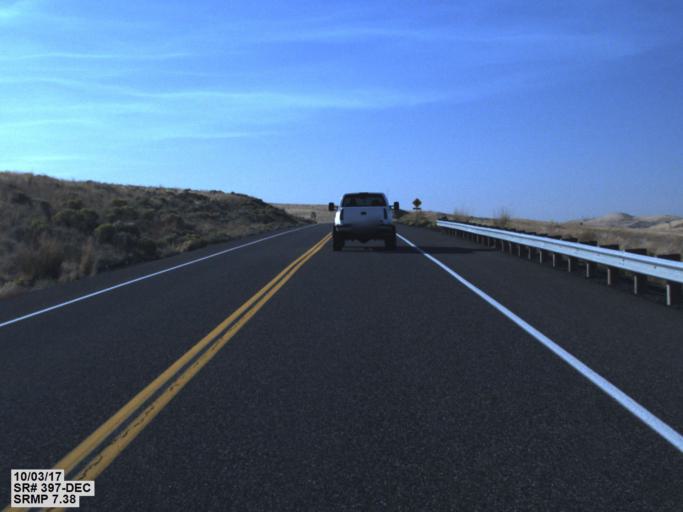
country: US
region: Washington
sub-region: Benton County
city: Finley
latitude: 46.1263
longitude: -119.0638
